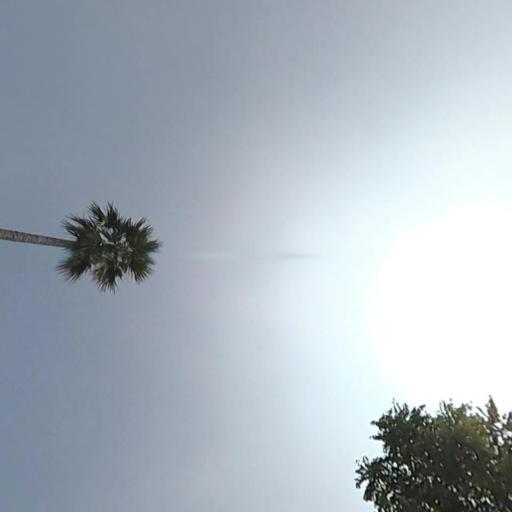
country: IN
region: Telangana
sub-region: Nalgonda
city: Nalgonda
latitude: 17.2122
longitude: 79.1573
